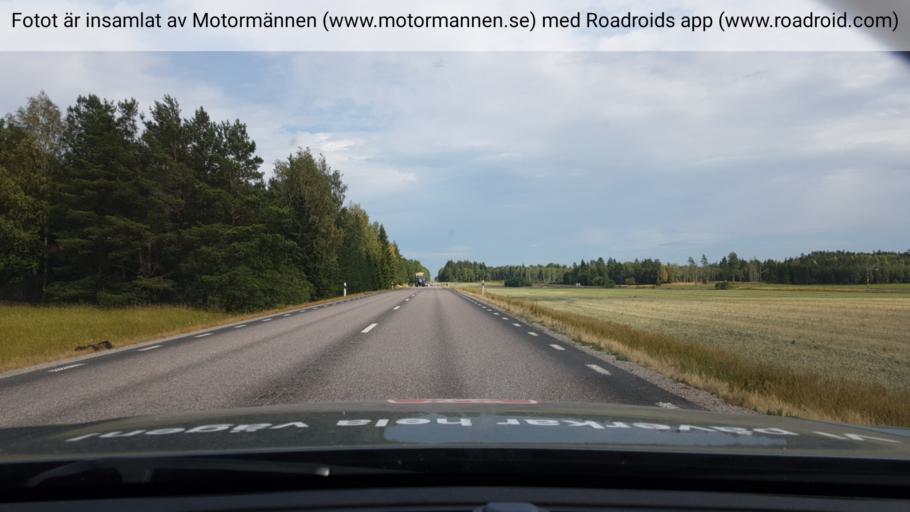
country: SE
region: Uppsala
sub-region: Enkopings Kommun
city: Orsundsbro
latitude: 59.8713
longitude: 17.3057
